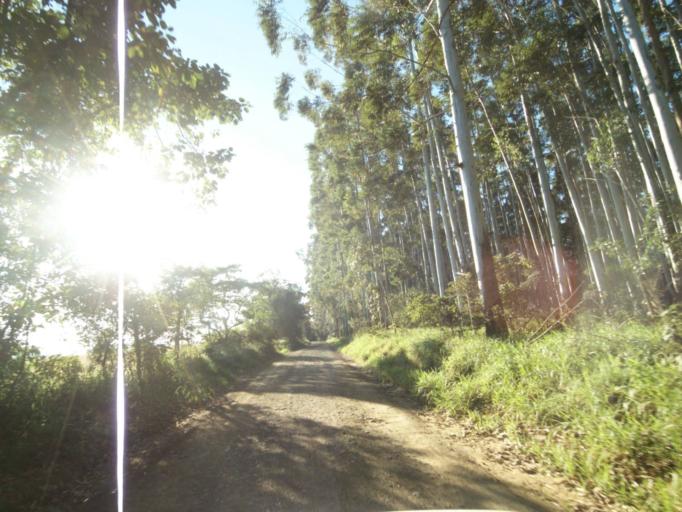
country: BR
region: Parana
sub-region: Tibagi
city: Tibagi
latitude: -24.5160
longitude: -50.6016
